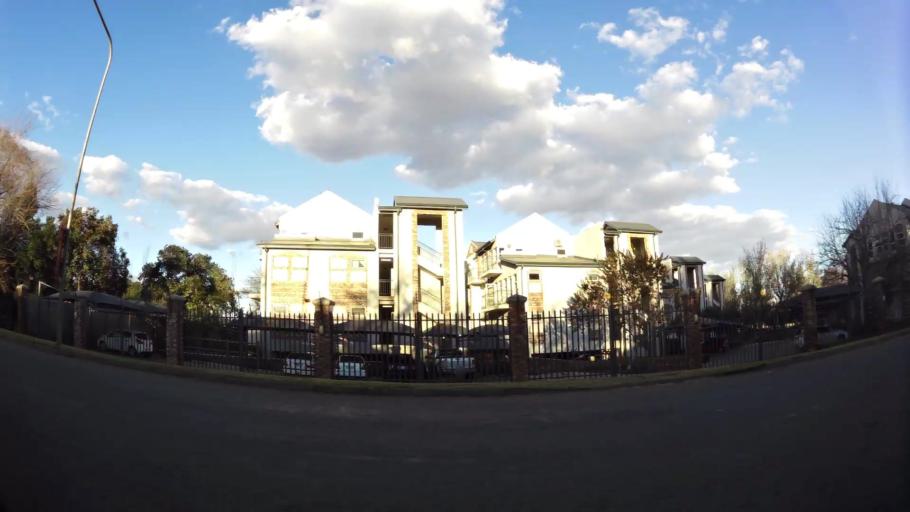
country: ZA
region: North-West
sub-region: Dr Kenneth Kaunda District Municipality
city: Potchefstroom
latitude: -26.6833
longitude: 27.1018
